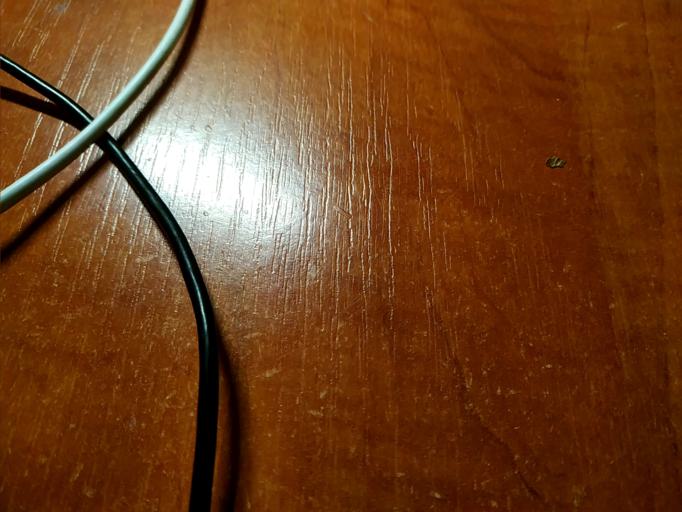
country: RU
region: Orjol
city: Naryshkino
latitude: 52.9851
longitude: 35.7029
